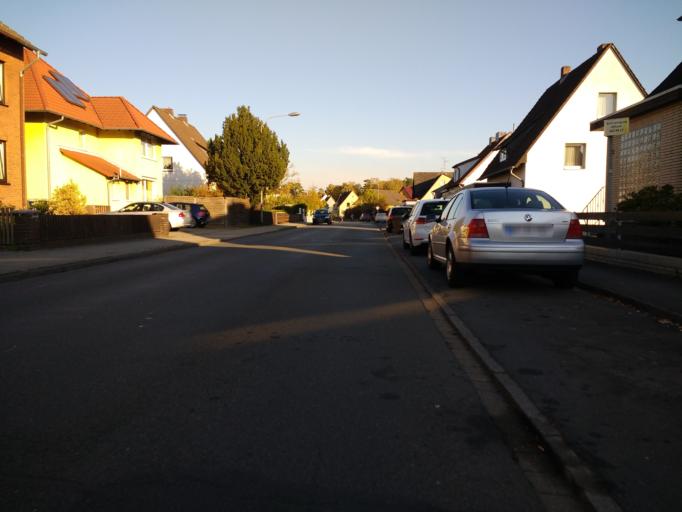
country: DE
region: Lower Saxony
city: Gifhorn
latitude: 52.4686
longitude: 10.5483
